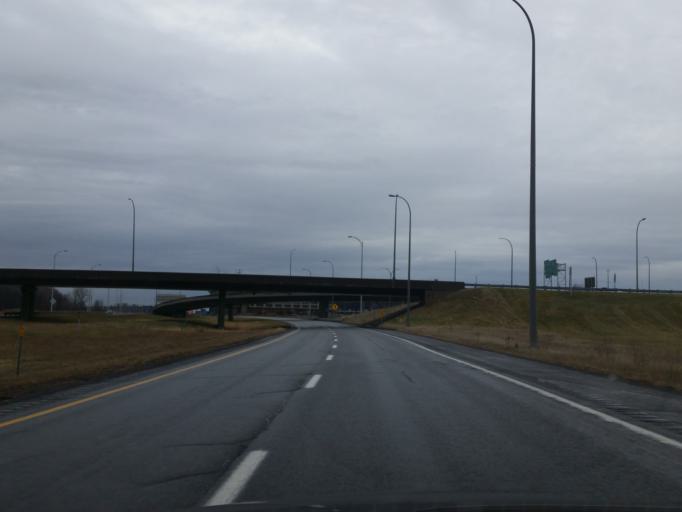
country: CA
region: Quebec
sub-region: Laurentides
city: Mirabel
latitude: 45.6821
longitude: -74.0386
